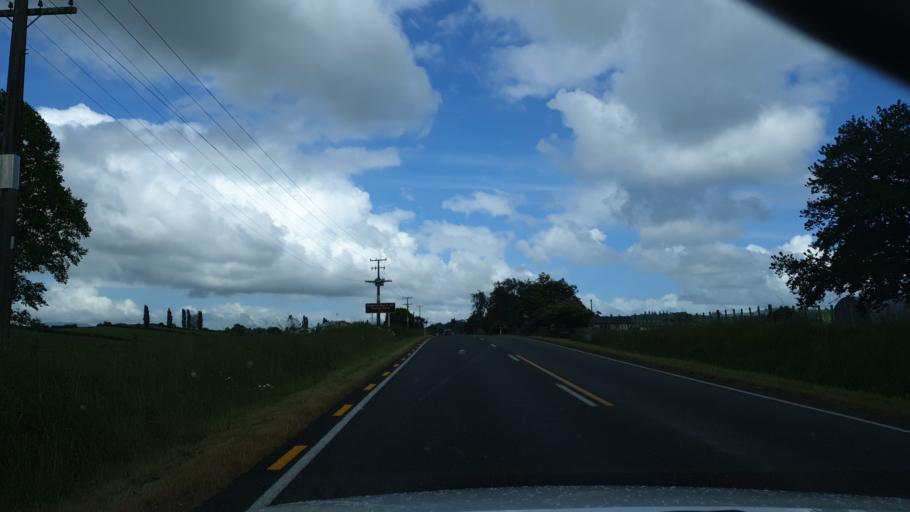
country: NZ
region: Waikato
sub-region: Matamata-Piako District
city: Matamata
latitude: -37.8755
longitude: 175.7230
